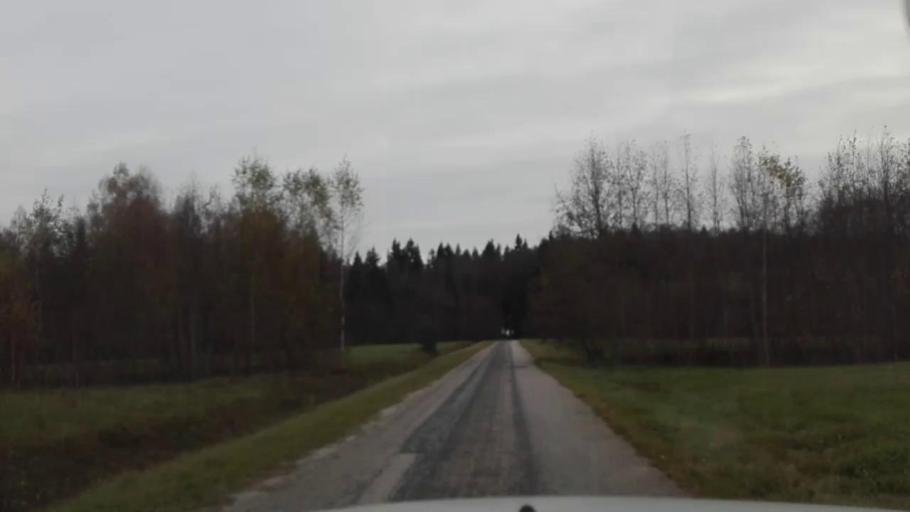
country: EE
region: Jogevamaa
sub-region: Poltsamaa linn
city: Poltsamaa
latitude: 58.4104
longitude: 26.0094
